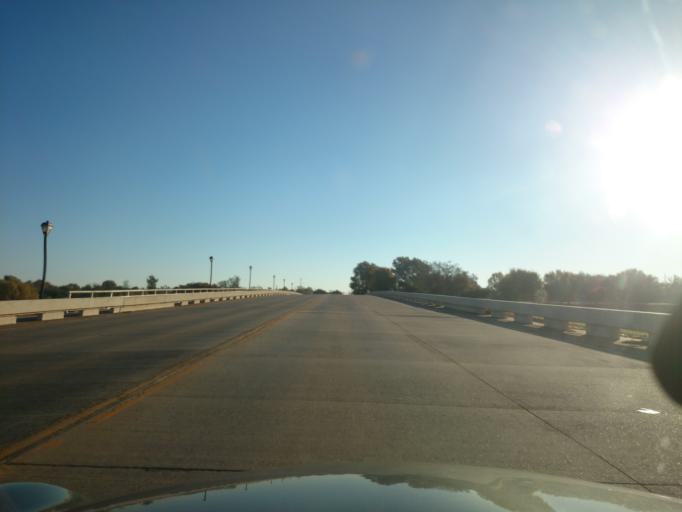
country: US
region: Oklahoma
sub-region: Payne County
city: Stillwater
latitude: 36.1450
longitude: -97.0645
